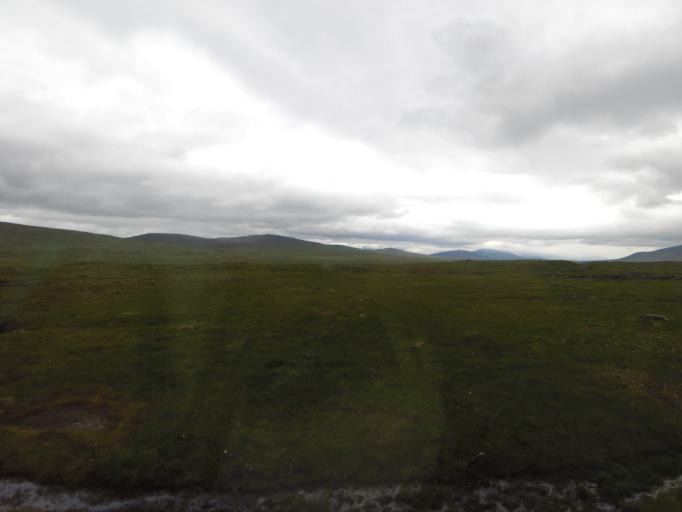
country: GB
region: Scotland
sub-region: Highland
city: Spean Bridge
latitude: 56.7193
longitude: -4.6203
